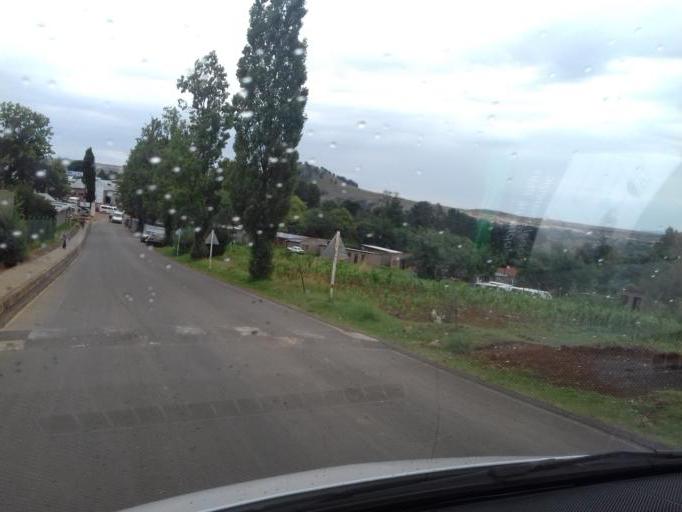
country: LS
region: Berea
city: Teyateyaneng
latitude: -29.1043
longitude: 27.9576
